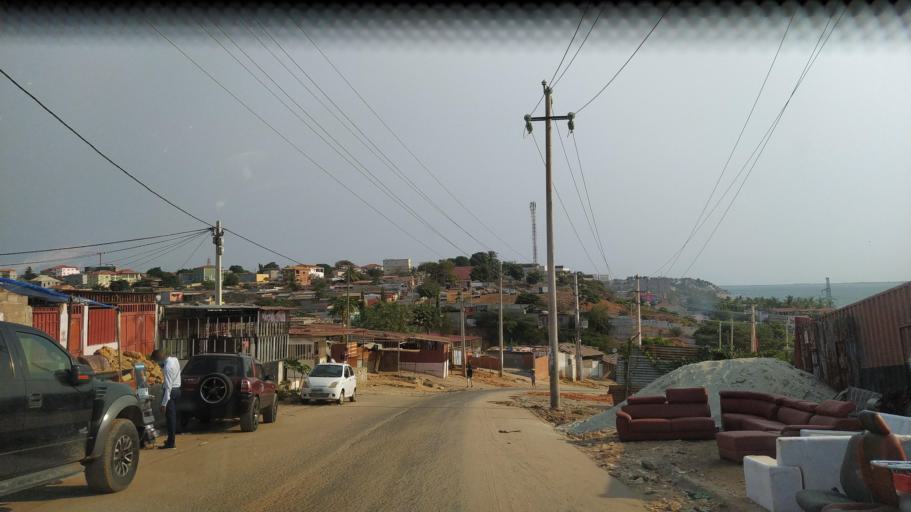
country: AO
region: Luanda
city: Luanda
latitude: -8.8704
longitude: 13.1984
